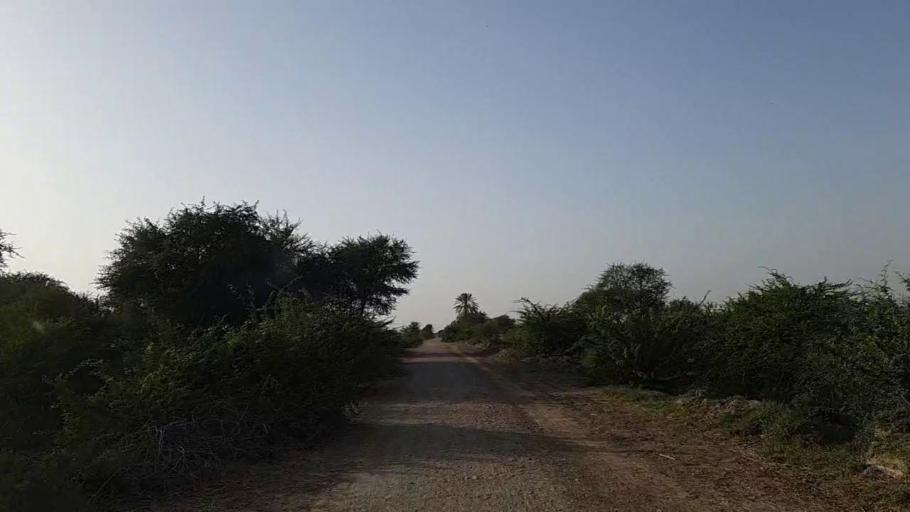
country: PK
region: Sindh
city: Jati
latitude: 24.3450
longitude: 68.1437
